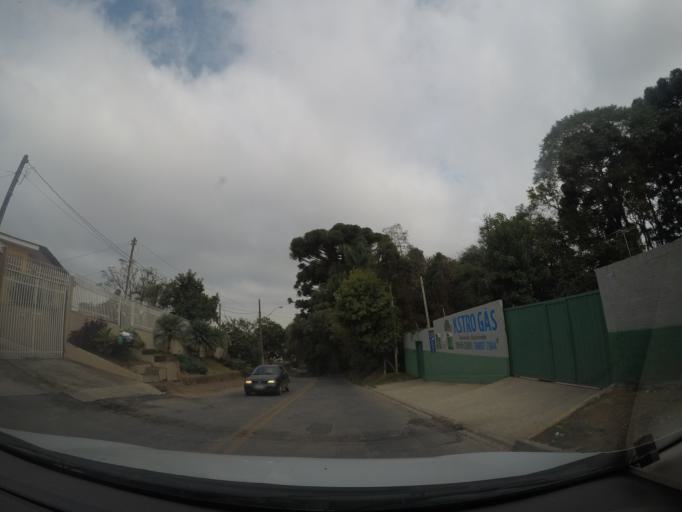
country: BR
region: Parana
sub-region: Colombo
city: Colombo
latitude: -25.3502
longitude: -49.2091
